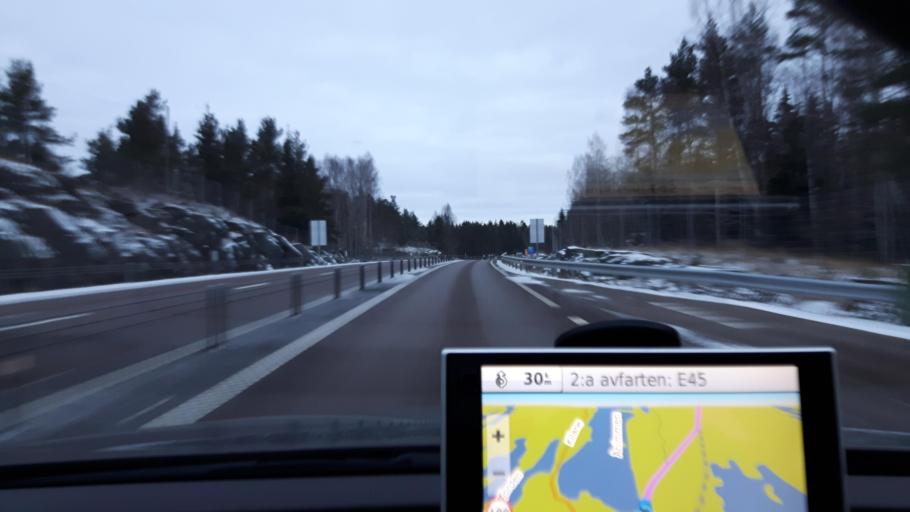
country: SE
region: Vaestra Goetaland
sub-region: Melleruds Kommun
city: Mellerud
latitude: 58.8201
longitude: 12.5229
